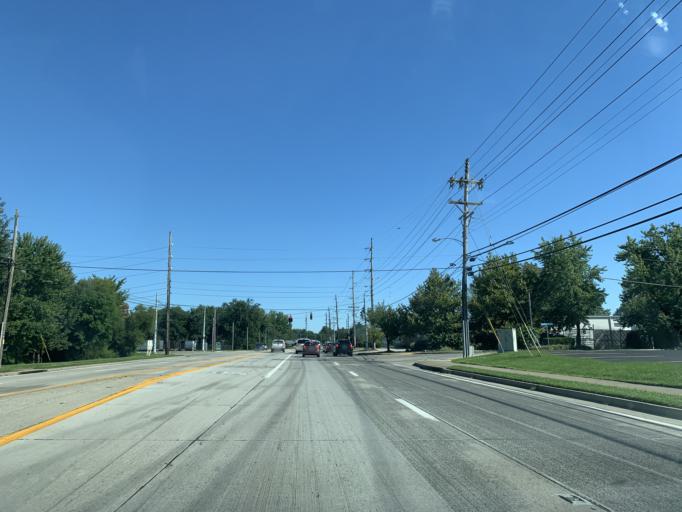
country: US
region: Kentucky
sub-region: Jefferson County
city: West Buechel
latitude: 38.1796
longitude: -85.6929
